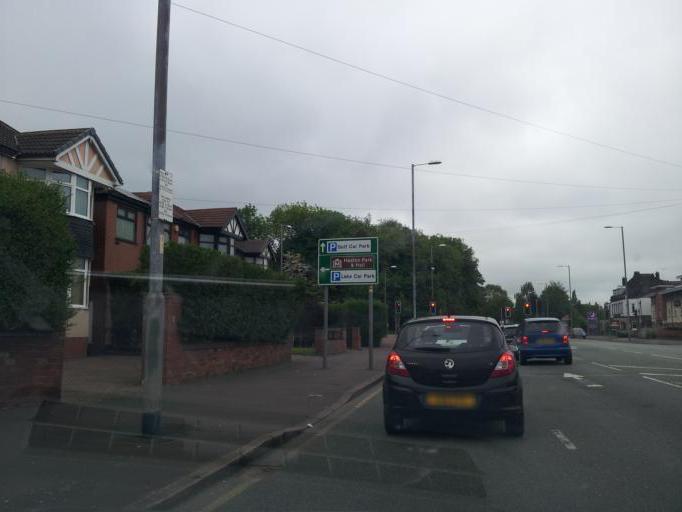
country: GB
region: England
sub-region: Manchester
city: Crumpsall
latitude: 53.5285
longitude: -2.2468
